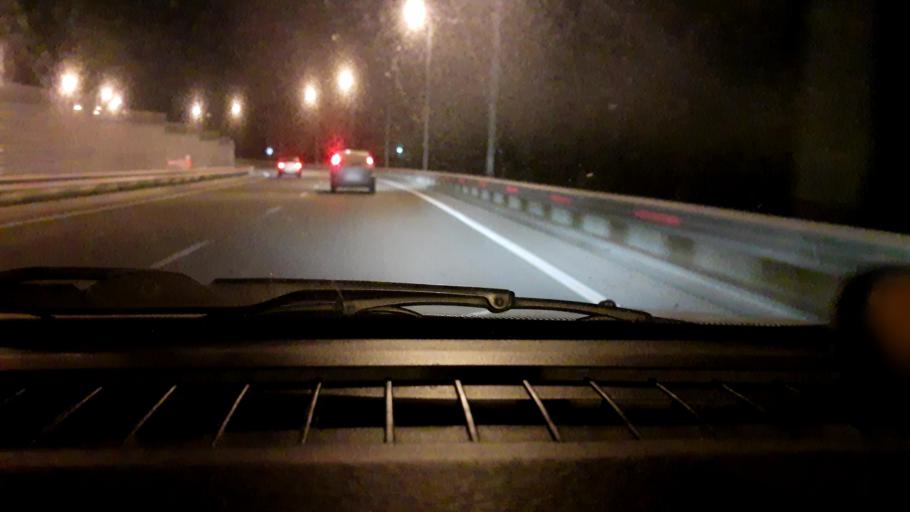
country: RU
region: Nizjnij Novgorod
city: Gorbatovka
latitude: 56.2455
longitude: 43.8079
